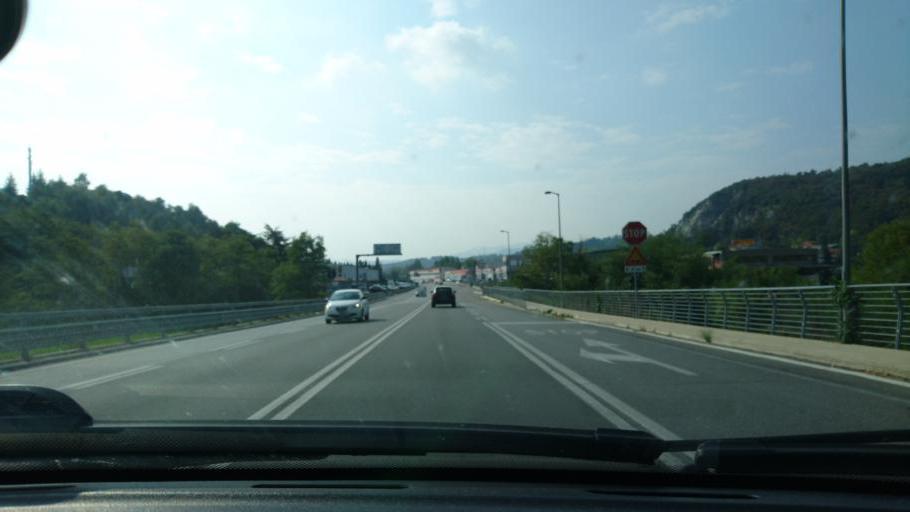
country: IT
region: Liguria
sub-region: Provincia di Savona
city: Cairo Montenotte
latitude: 44.3928
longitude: 8.2818
